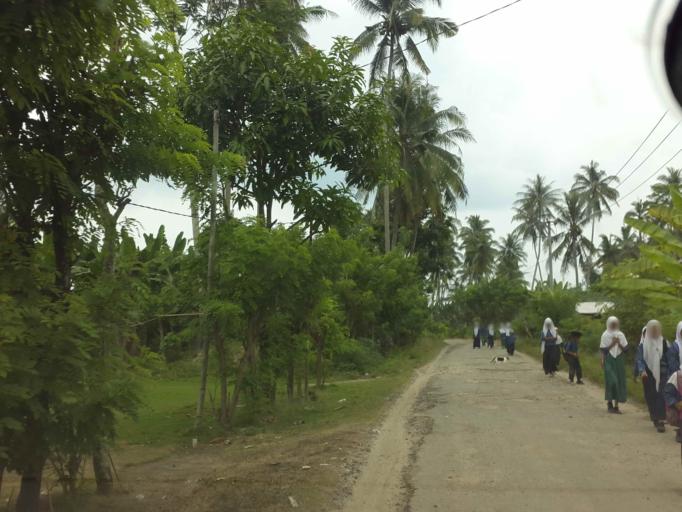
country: ID
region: Lampung
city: Sidorejo
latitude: -5.6347
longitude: 105.4511
